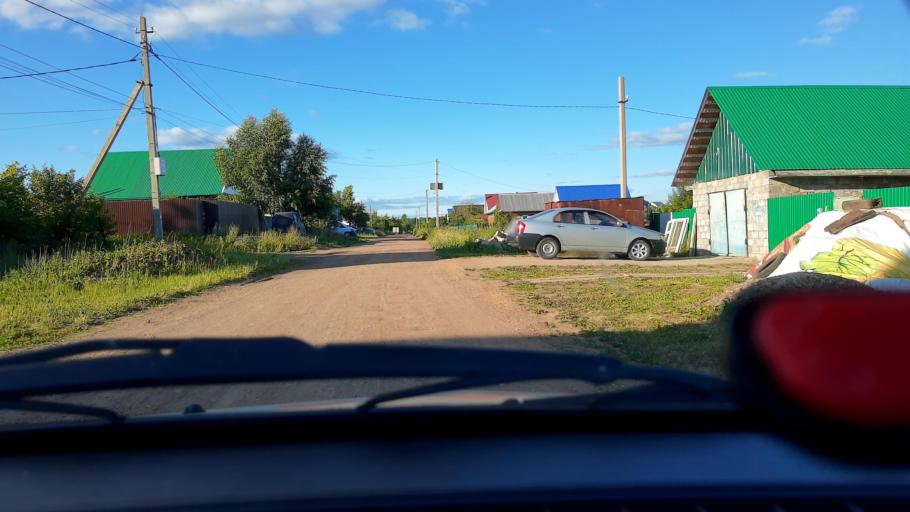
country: RU
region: Bashkortostan
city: Iglino
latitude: 54.7795
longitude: 56.2418
